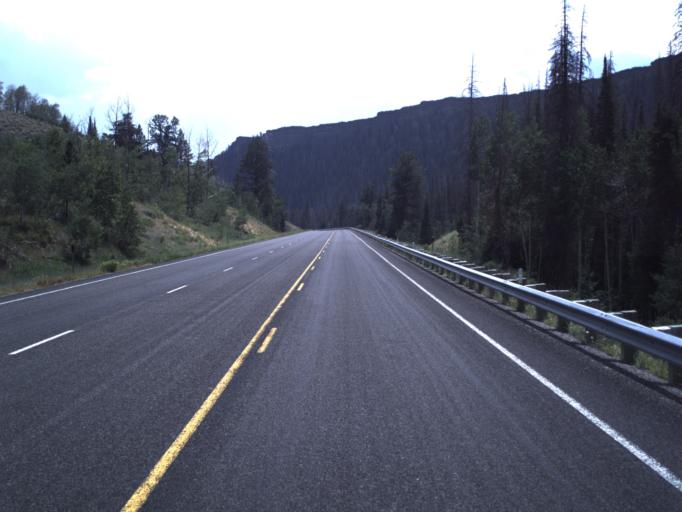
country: US
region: Utah
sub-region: Summit County
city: Francis
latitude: 40.4815
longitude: -110.9441
